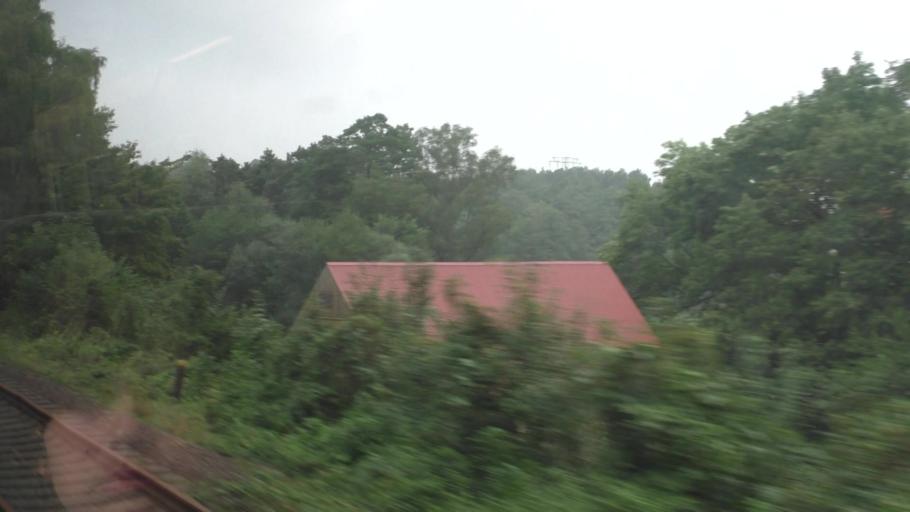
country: DE
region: Saxony
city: Arnsdorf
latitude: 51.1019
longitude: 13.9547
